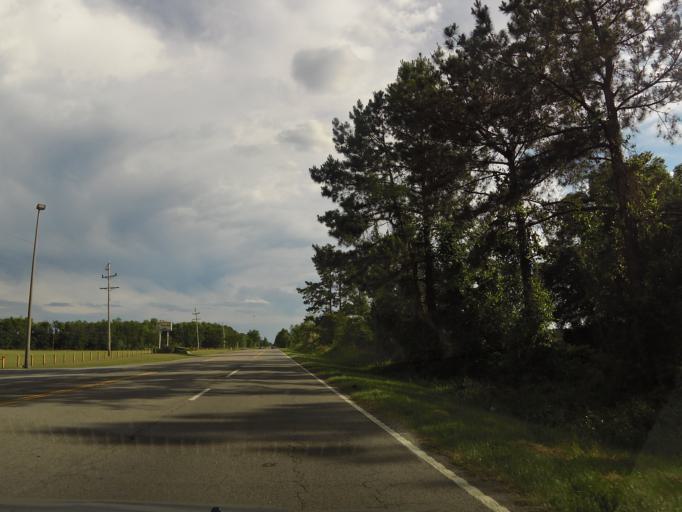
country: US
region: South Carolina
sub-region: Hampton County
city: Estill
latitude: 32.7913
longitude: -81.2405
